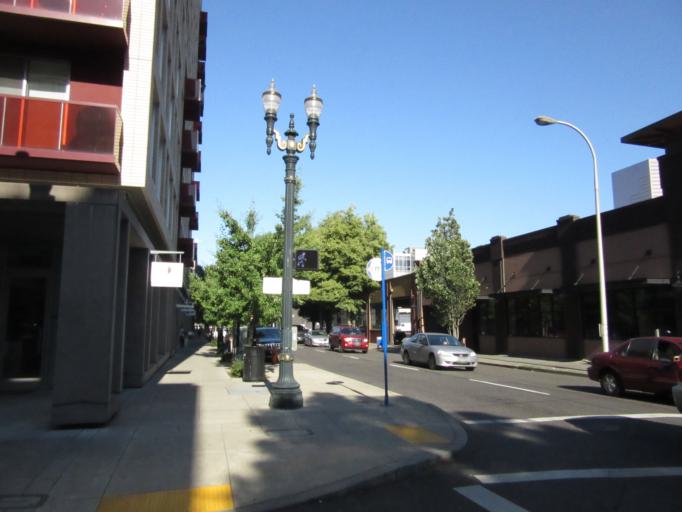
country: US
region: Oregon
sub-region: Multnomah County
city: Portland
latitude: 45.5266
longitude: -122.6813
